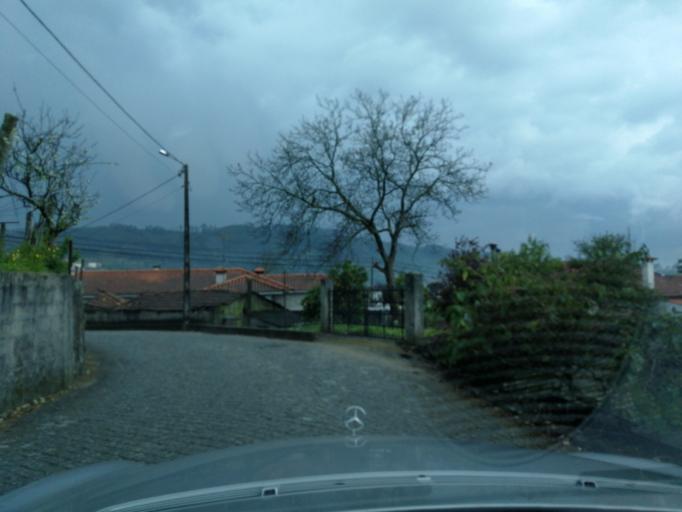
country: PT
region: Braga
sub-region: Braga
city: Oliveira
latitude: 41.4520
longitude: -8.4600
